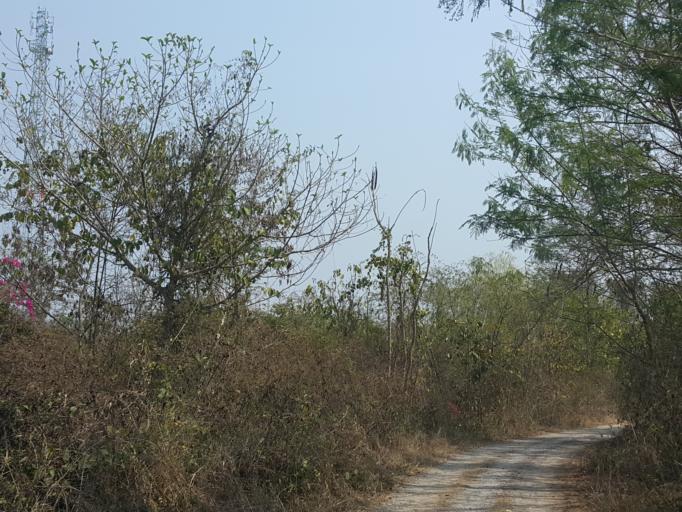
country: TH
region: Chiang Mai
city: Hang Dong
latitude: 18.6918
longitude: 98.8693
